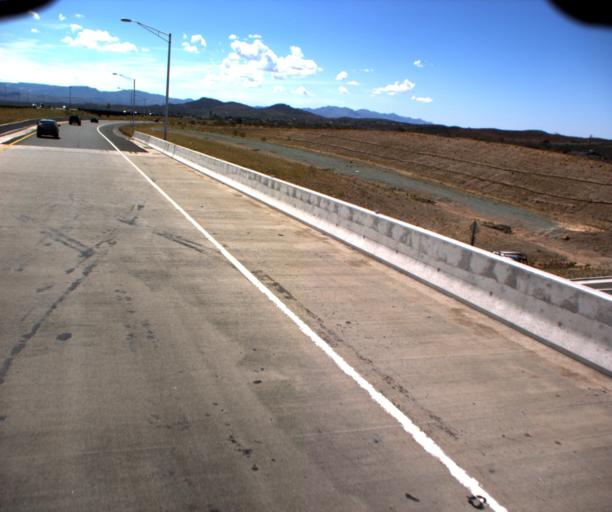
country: US
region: Arizona
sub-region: Yavapai County
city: Cordes Lakes
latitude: 34.3324
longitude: -112.1256
